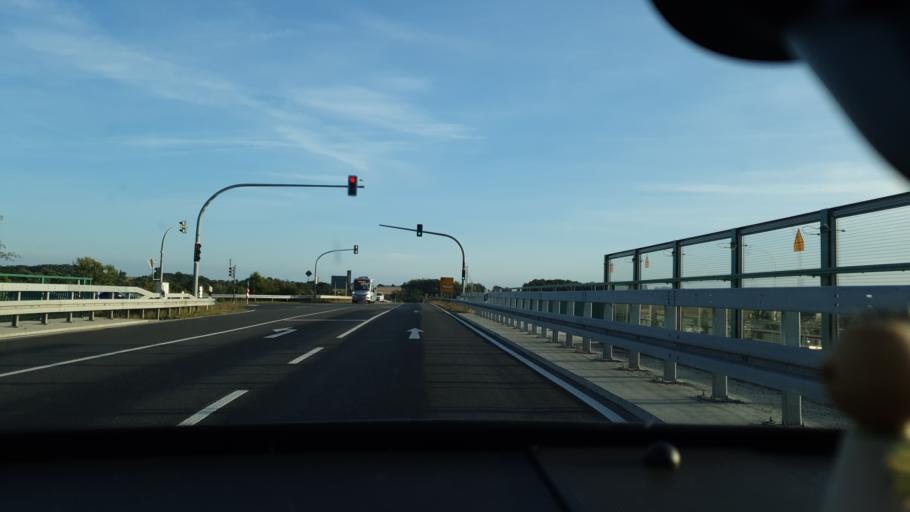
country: DE
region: Saxony
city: Eilenburg
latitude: 51.4448
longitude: 12.6137
